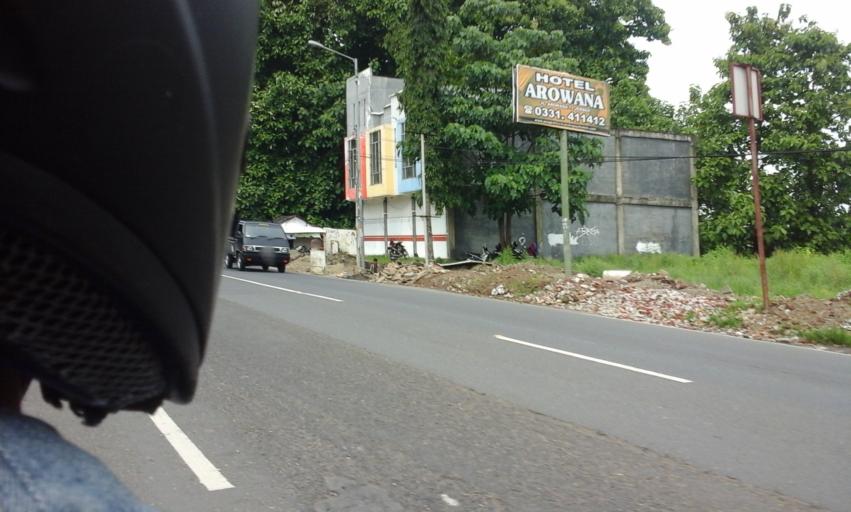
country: ID
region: East Java
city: Mangli
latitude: -8.1930
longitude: 113.6445
